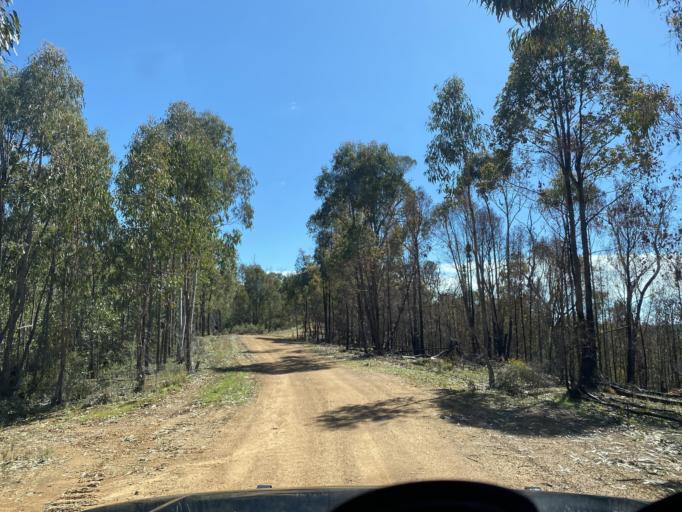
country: AU
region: Victoria
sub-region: Benalla
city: Benalla
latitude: -36.7351
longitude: 146.1822
